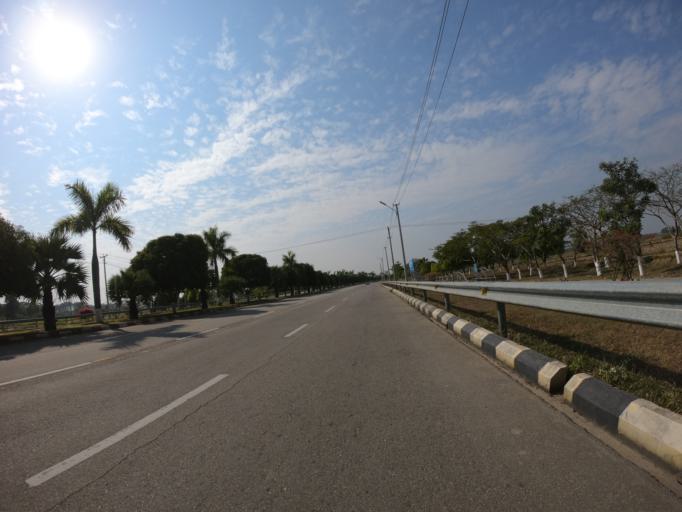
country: MM
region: Mandalay
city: Nay Pyi Taw
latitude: 19.6538
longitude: 96.1369
